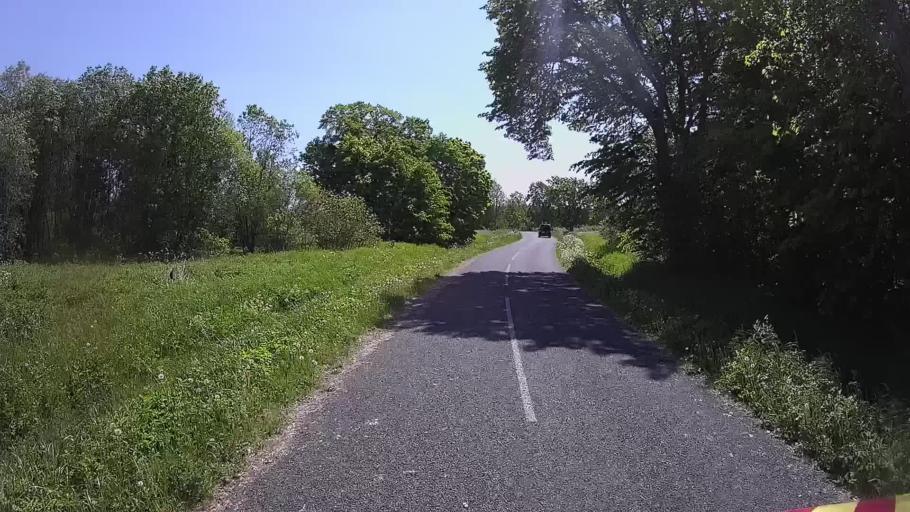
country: LV
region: Dundaga
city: Dundaga
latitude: 57.9361
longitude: 22.0935
